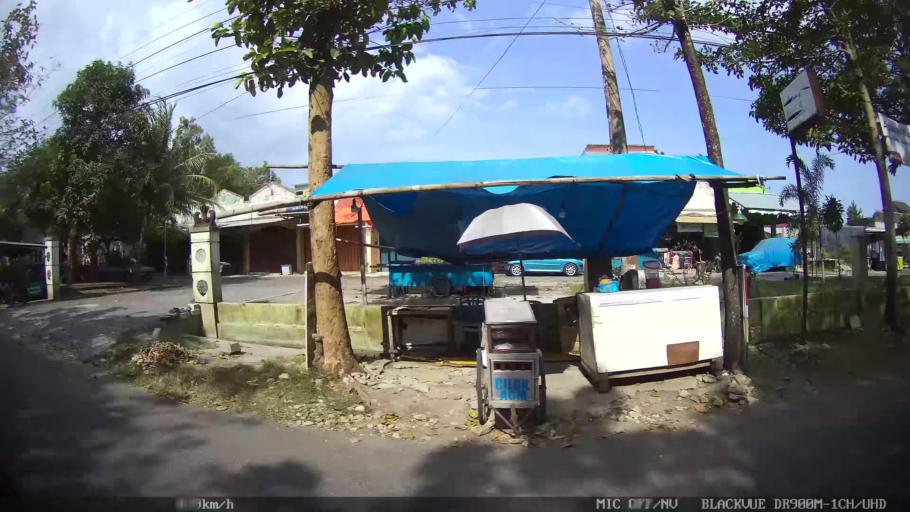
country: ID
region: Daerah Istimewa Yogyakarta
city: Kasihan
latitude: -7.8566
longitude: 110.3010
